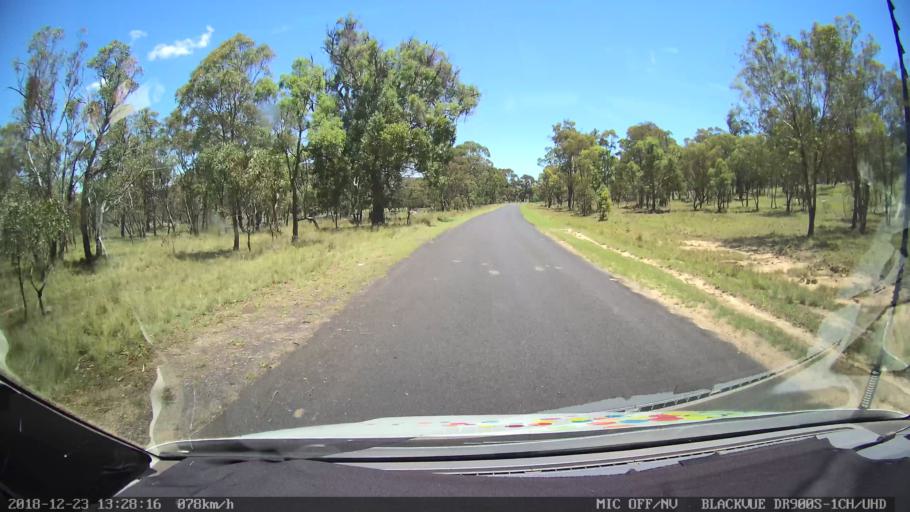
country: AU
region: New South Wales
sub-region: Armidale Dumaresq
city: Armidale
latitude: -30.4657
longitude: 151.3508
